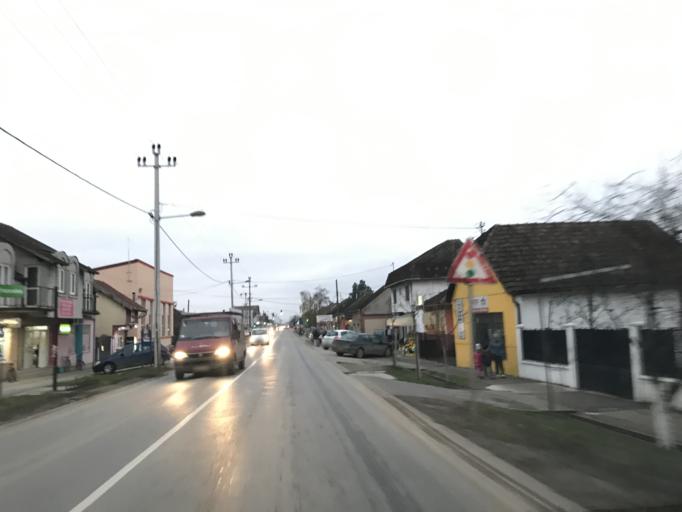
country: RS
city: Rumenka
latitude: 45.2924
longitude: 19.7421
